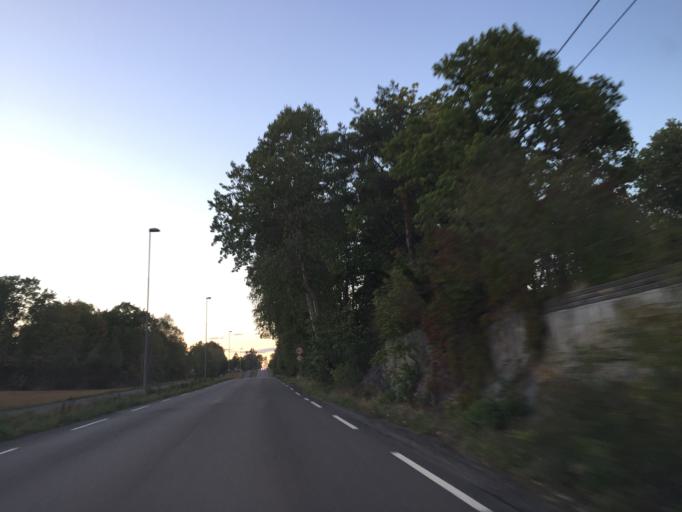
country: NO
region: Ostfold
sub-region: Moss
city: Moss
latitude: 59.4960
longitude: 10.6880
